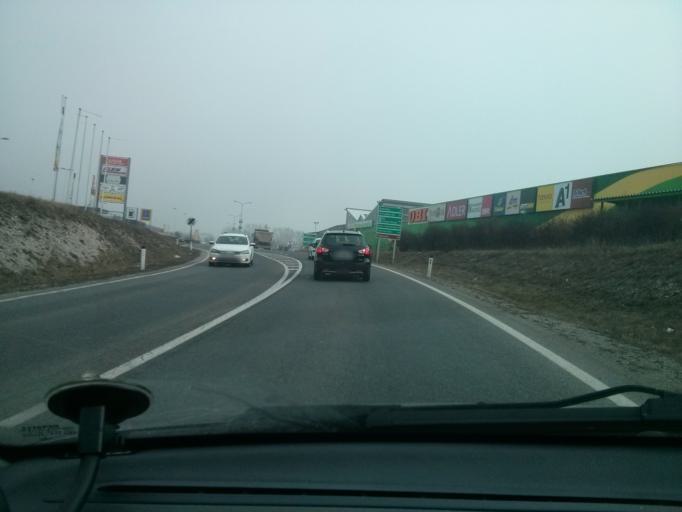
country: AT
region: Lower Austria
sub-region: Politischer Bezirk Wiener Neustadt
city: Theresienfeld
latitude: 47.8463
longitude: 16.2424
